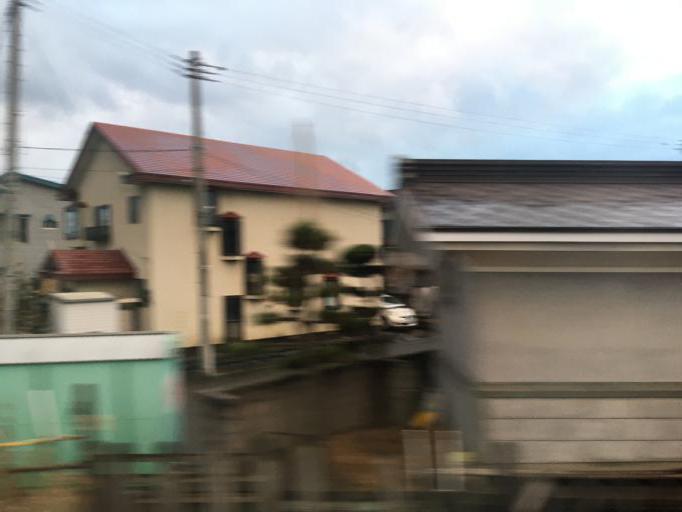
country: JP
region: Aomori
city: Aomori Shi
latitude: 40.8251
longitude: 140.7214
